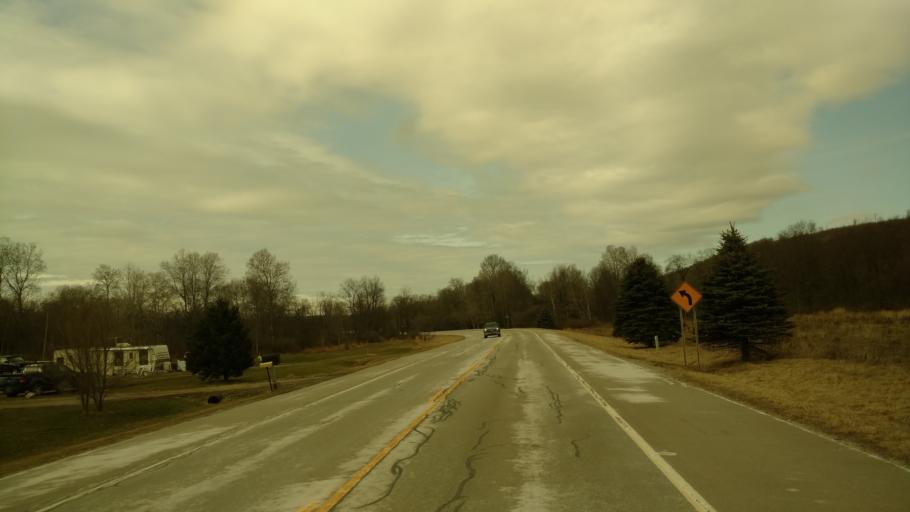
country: US
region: New York
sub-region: Allegany County
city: Wellsville
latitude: 42.0117
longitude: -77.8907
